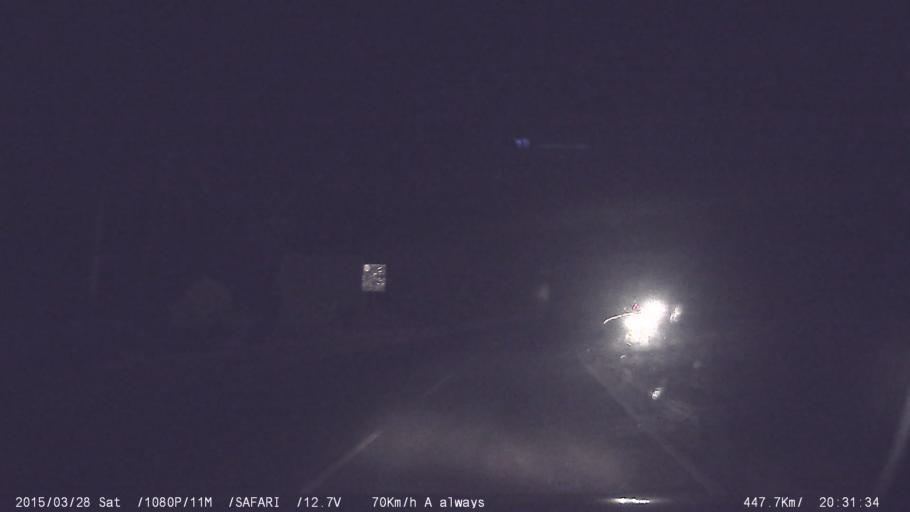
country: IN
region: Karnataka
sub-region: Mandya
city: Maddur
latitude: 12.6171
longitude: 77.0859
